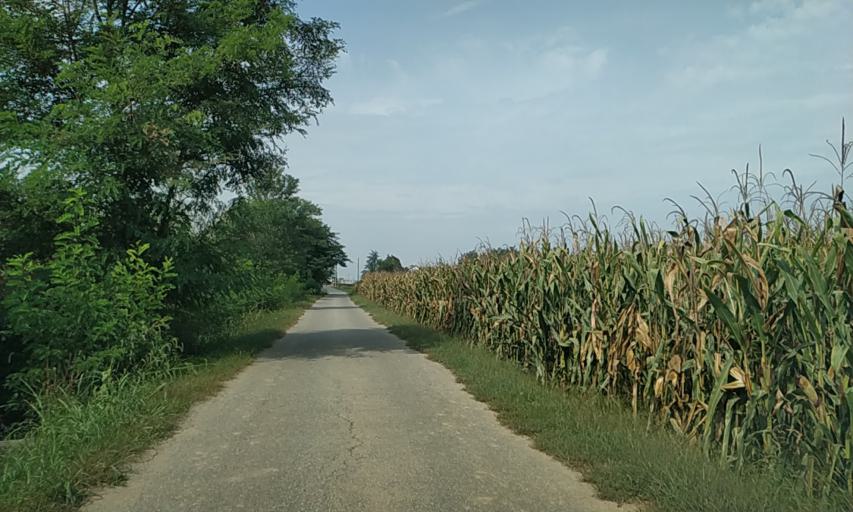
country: IT
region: Piedmont
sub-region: Provincia di Vercelli
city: Livorno Ferraris
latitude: 45.3080
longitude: 8.0838
